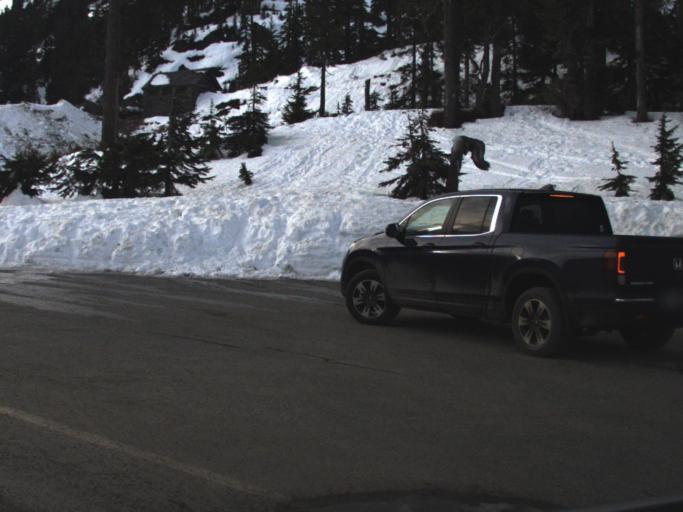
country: CA
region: British Columbia
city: Agassiz
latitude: 48.8641
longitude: -121.6808
